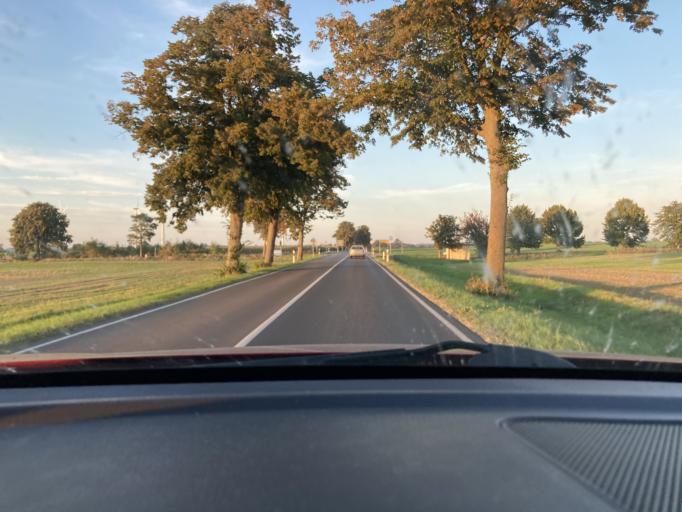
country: DE
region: Mecklenburg-Vorpommern
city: Alt-Sanitz
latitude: 53.7645
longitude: 13.6436
